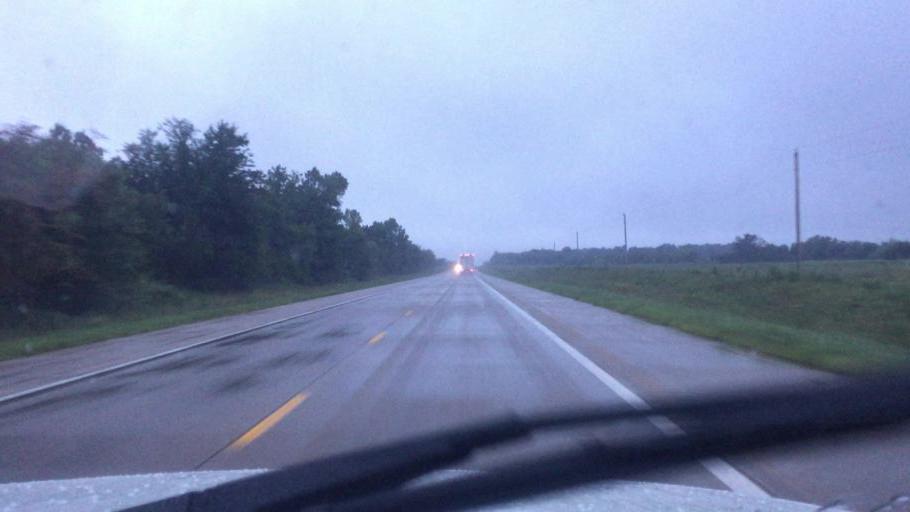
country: US
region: Kansas
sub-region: Neosho County
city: Chanute
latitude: 37.5542
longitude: -95.4709
